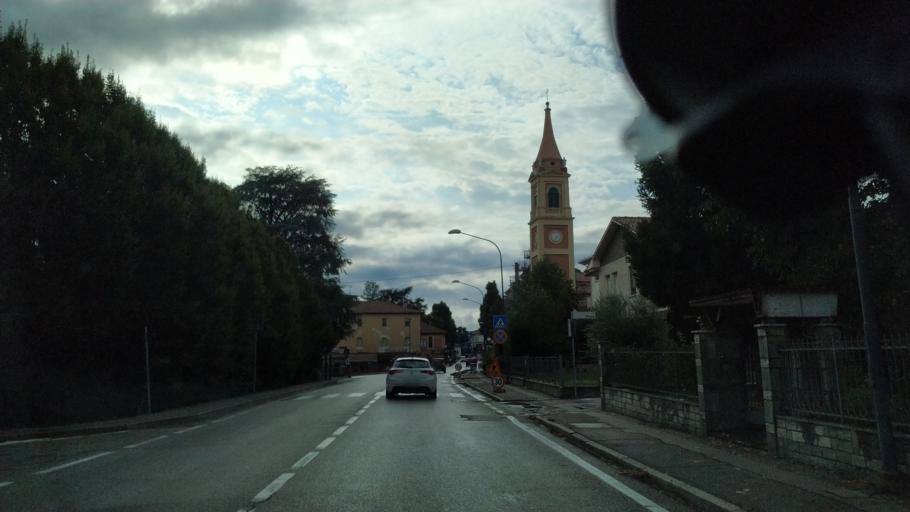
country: IT
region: Emilia-Romagna
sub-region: Provincia di Ferrara
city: Sant'Agostino
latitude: 44.7925
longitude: 11.3880
